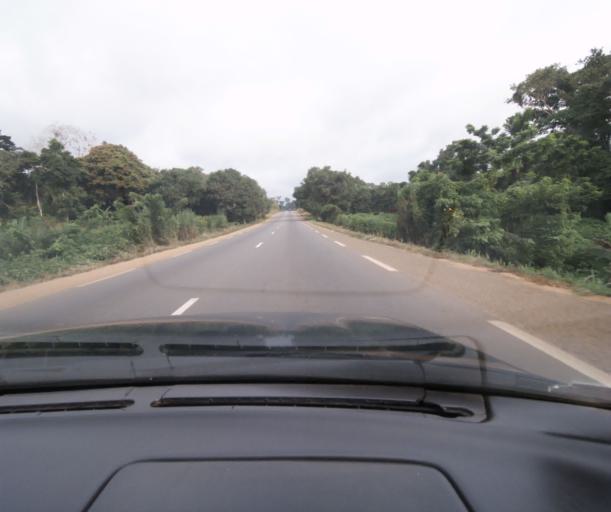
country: CM
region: Centre
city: Obala
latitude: 4.1078
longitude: 11.5334
